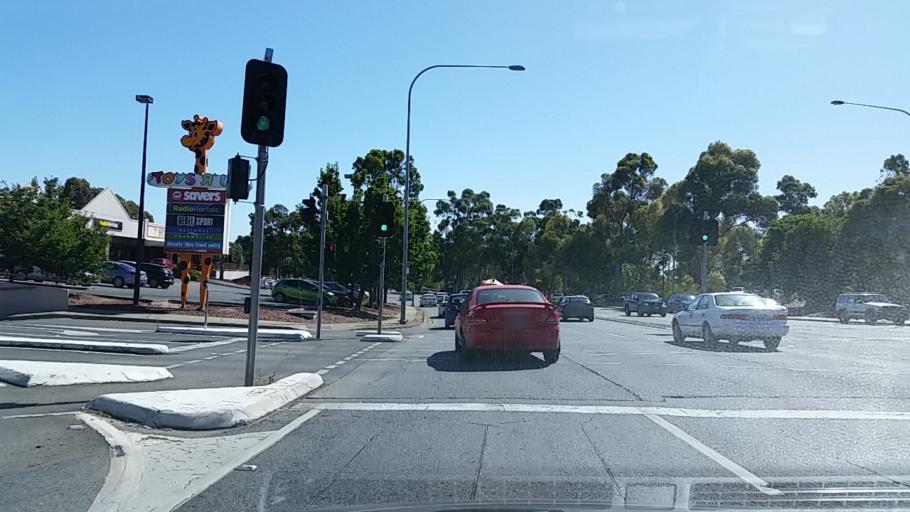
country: AU
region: South Australia
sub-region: Tea Tree Gully
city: Hope Valley
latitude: -34.8287
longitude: 138.6918
